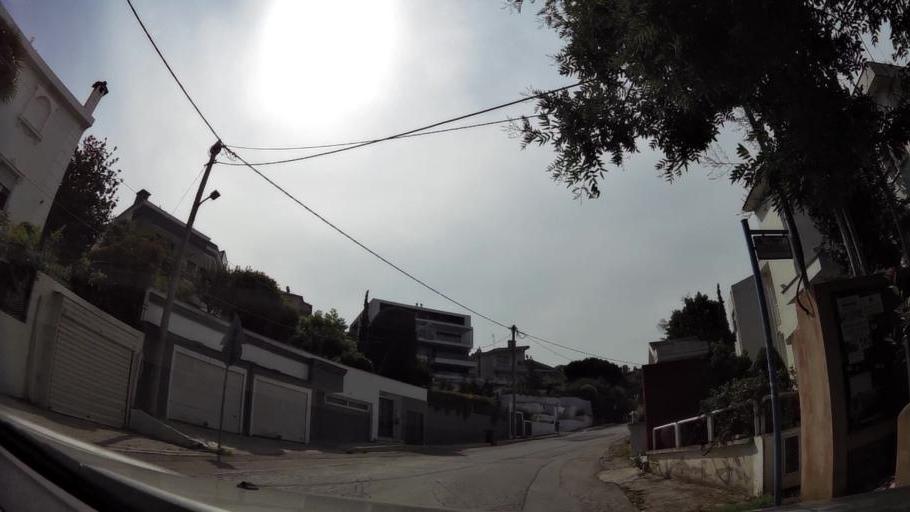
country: GR
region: Central Macedonia
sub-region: Nomos Thessalonikis
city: Panorama
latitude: 40.5807
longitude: 23.0197
